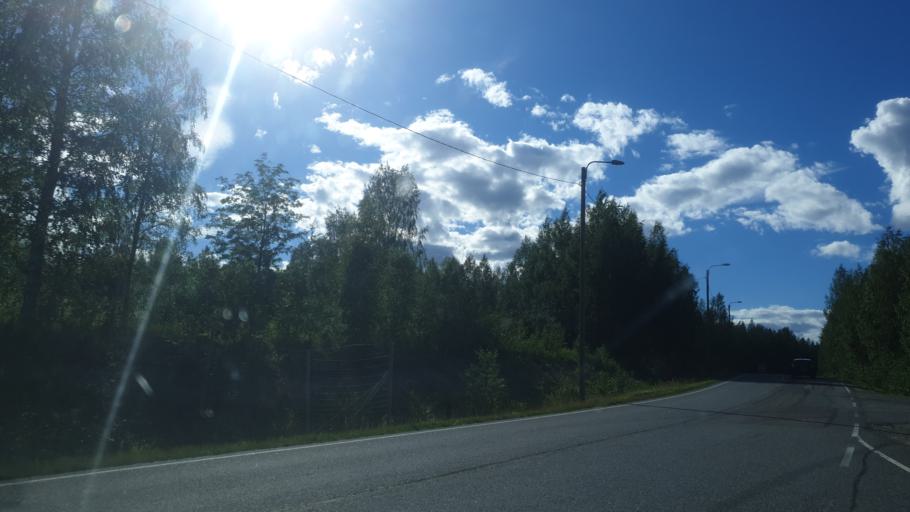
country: FI
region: Southern Savonia
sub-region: Mikkeli
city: Maentyharju
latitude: 61.4798
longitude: 26.7480
